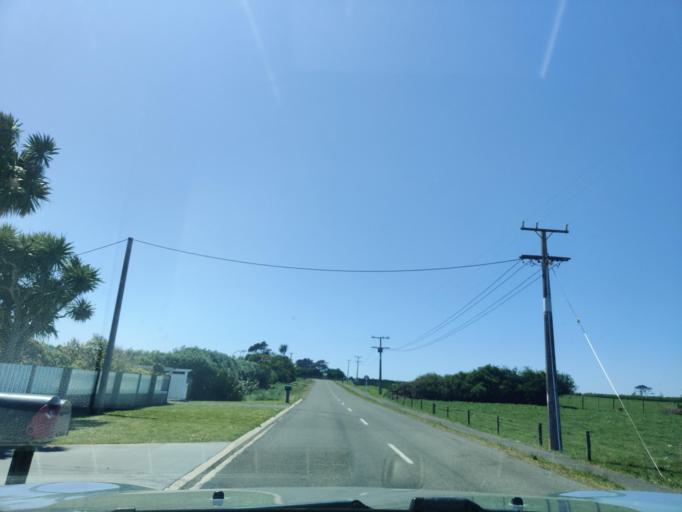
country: NZ
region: Taranaki
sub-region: South Taranaki District
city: Hawera
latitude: -39.5987
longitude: 174.2649
